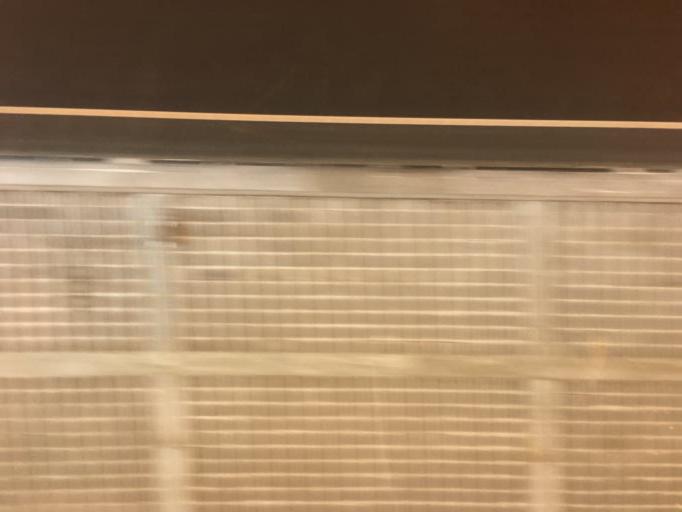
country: PT
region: Lisbon
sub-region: Odivelas
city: Pontinha
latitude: 38.7656
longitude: -9.2051
